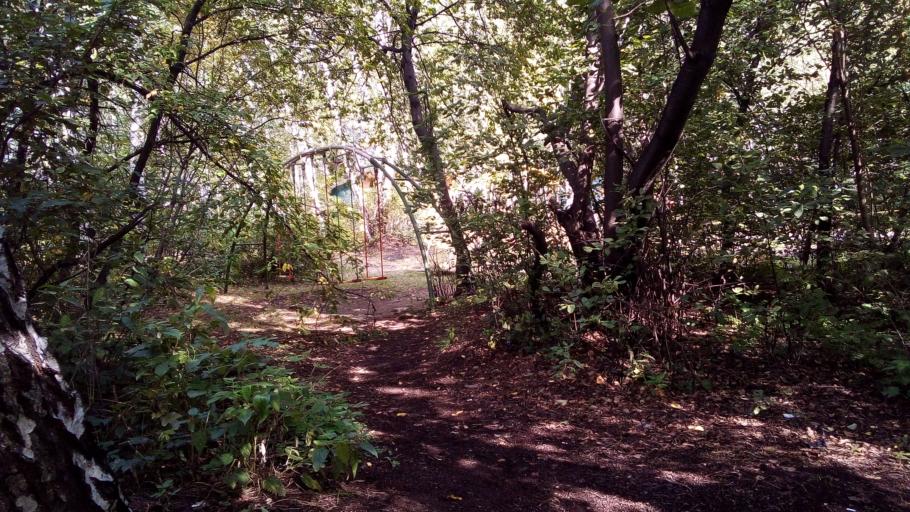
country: RU
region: Chelyabinsk
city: Tayginka
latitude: 55.4784
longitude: 60.4946
